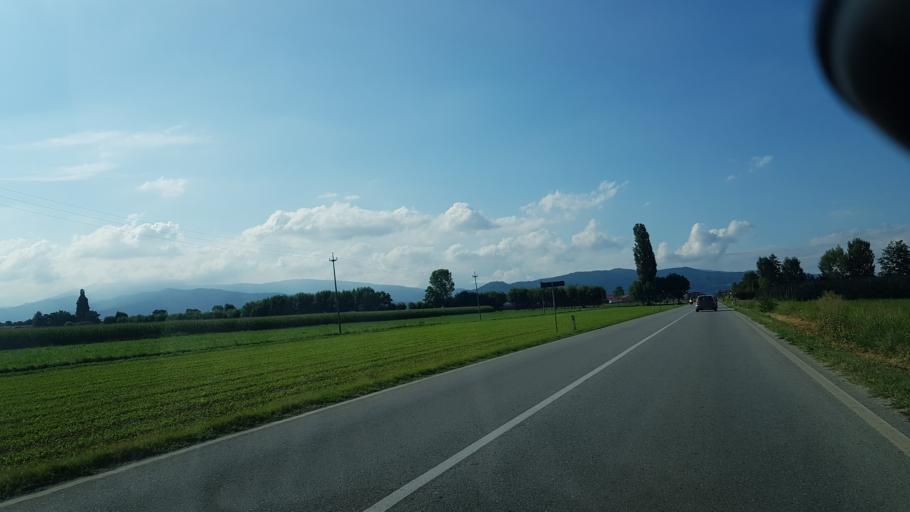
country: IT
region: Piedmont
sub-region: Provincia di Cuneo
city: Roata Rossi
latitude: 44.4655
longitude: 7.5153
